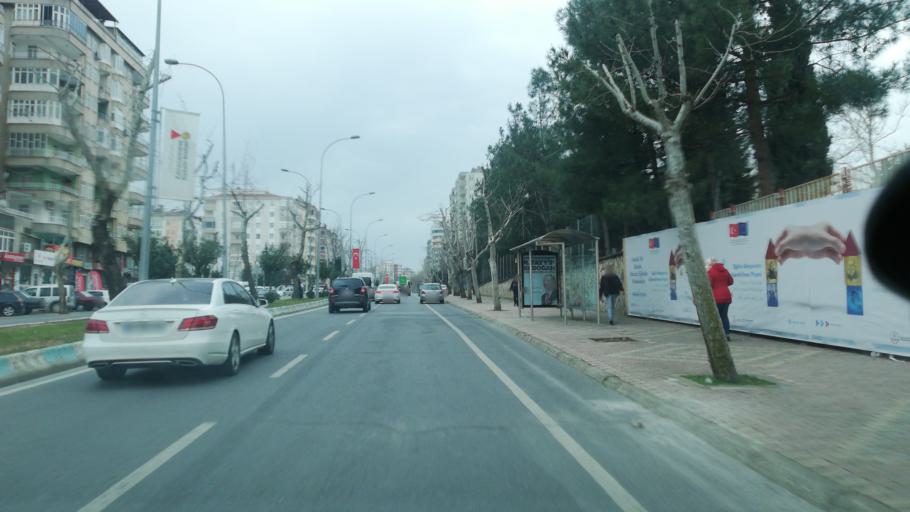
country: TR
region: Kahramanmaras
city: Kahramanmaras
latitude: 37.5867
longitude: 36.9031
